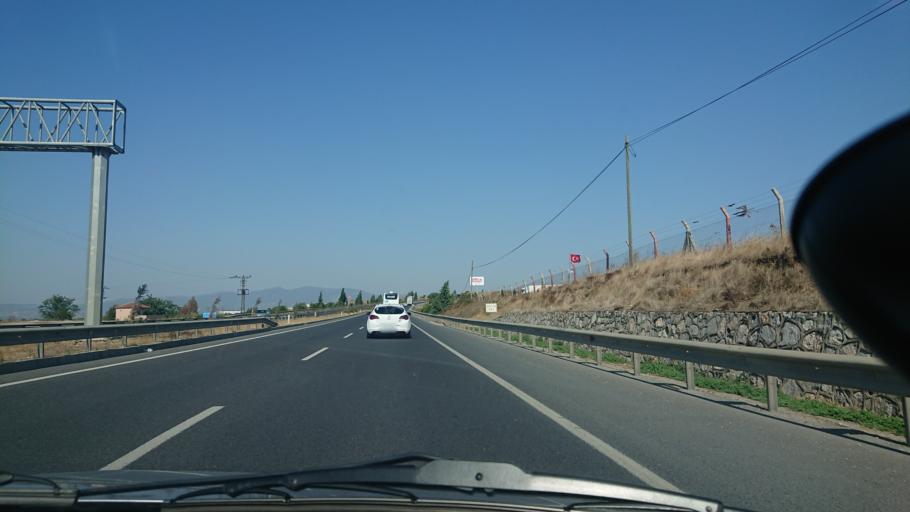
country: TR
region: Manisa
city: Karaoglanli
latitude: 38.4822
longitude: 27.6120
